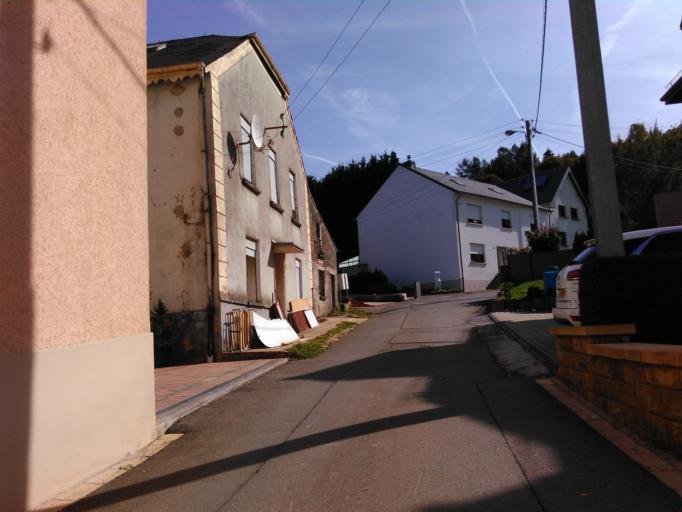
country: LU
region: Luxembourg
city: Tetange
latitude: 49.4731
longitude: 6.0405
